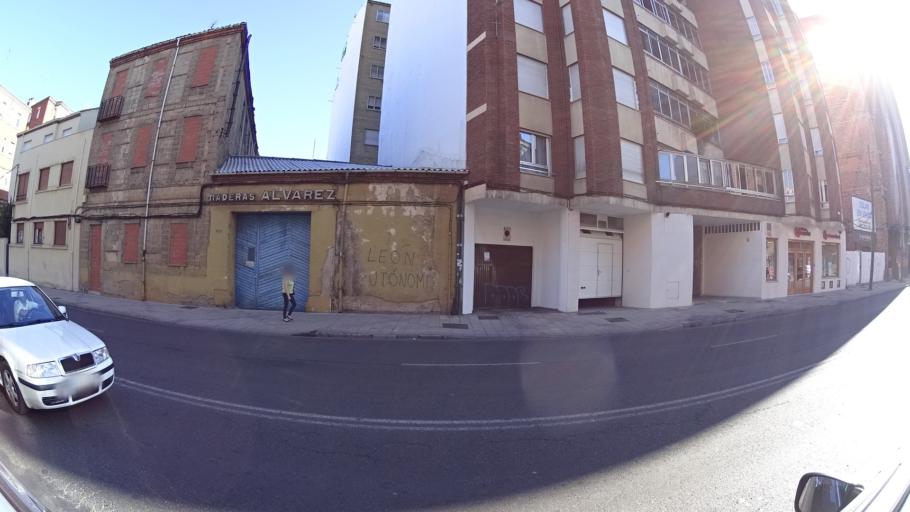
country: ES
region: Castille and Leon
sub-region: Provincia de Leon
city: Leon
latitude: 42.6043
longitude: -5.5761
